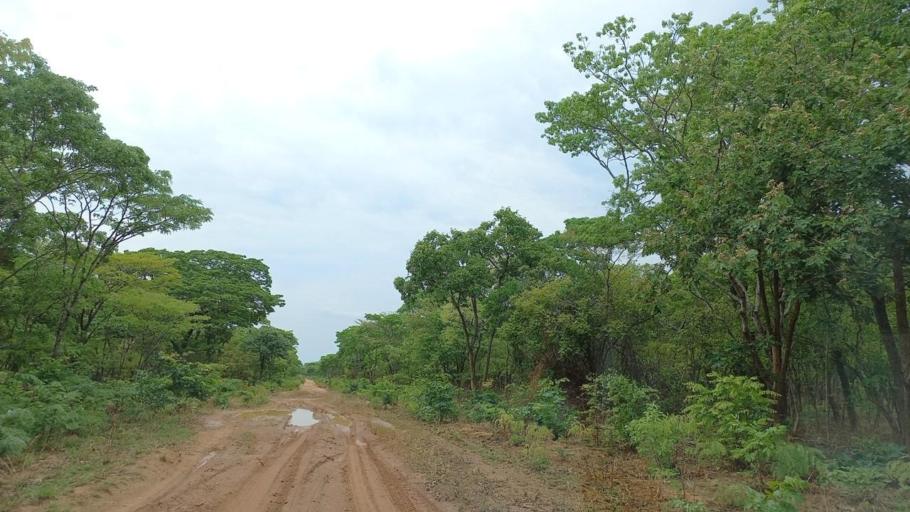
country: ZM
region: North-Western
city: Kalengwa
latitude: -13.5870
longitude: 24.9721
